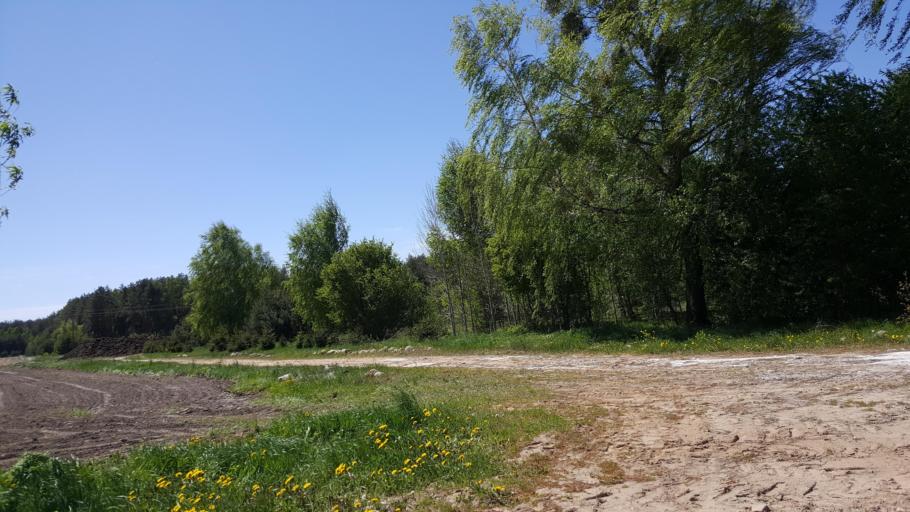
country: BY
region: Brest
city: Kamyanyuki
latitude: 52.4819
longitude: 23.7973
